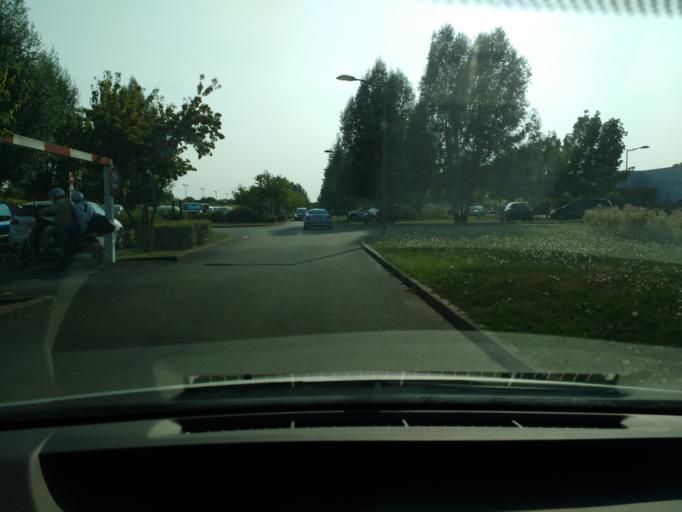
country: FR
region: Pays de la Loire
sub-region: Departement de la Sarthe
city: La Fleche
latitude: 47.7030
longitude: -0.0483
